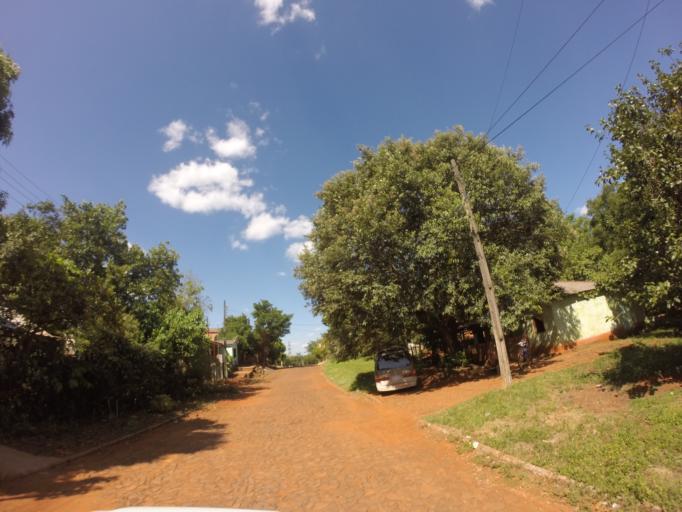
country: PY
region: Alto Parana
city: Ciudad del Este
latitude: -25.4330
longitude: -54.6396
